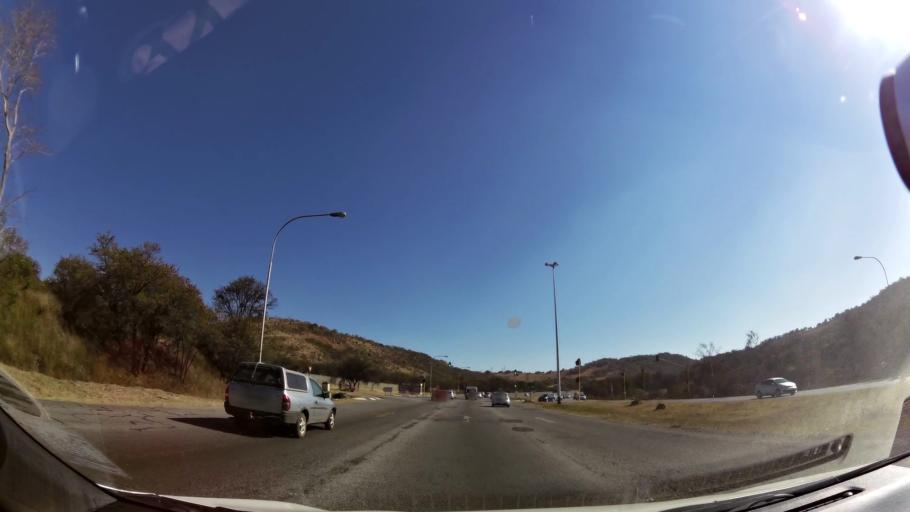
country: ZA
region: Gauteng
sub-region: City of Johannesburg Metropolitan Municipality
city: Johannesburg
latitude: -26.2873
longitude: 28.0365
